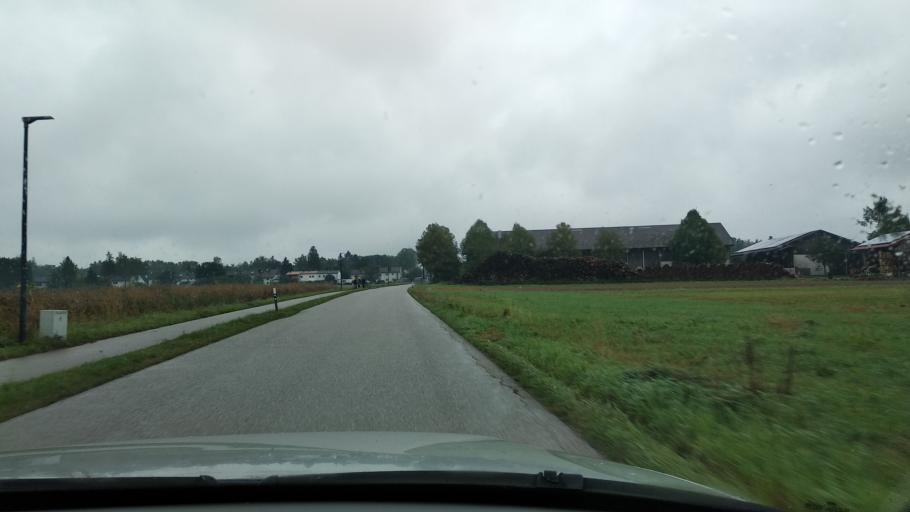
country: DE
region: Bavaria
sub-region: Upper Bavaria
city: Hohenbrunn
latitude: 48.0385
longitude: 11.7047
